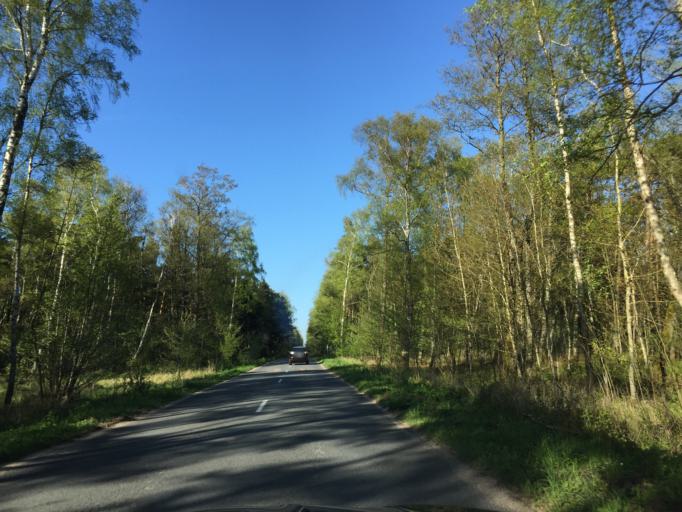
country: LT
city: Nida
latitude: 55.2164
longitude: 20.8845
